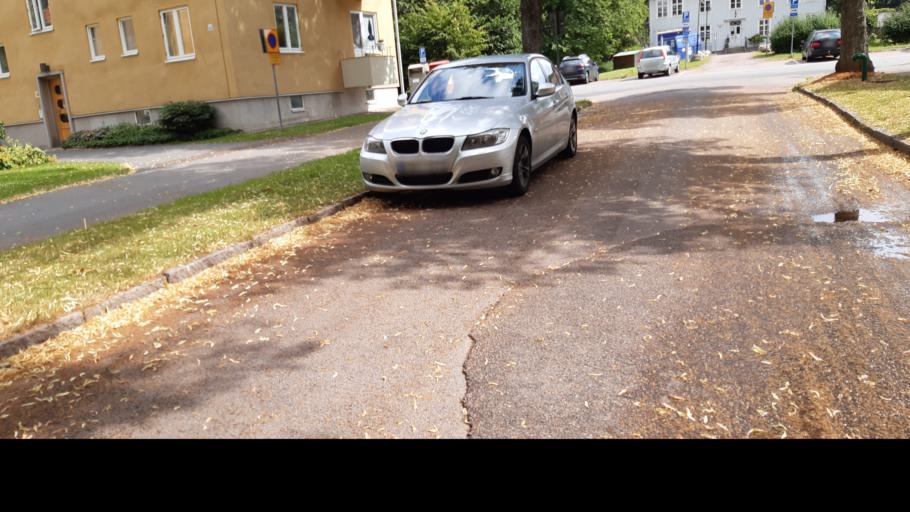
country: SE
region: Vaestra Goetaland
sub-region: Goteborg
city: Eriksbo
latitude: 57.7226
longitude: 12.0362
